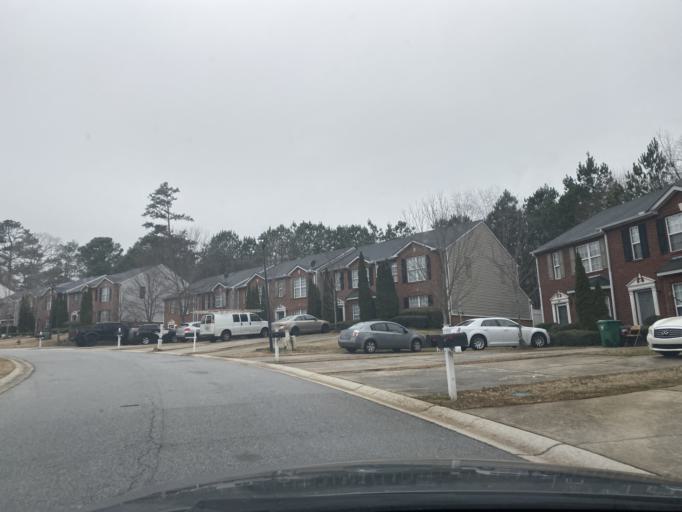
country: US
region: Georgia
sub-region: DeKalb County
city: Pine Mountain
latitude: 33.7003
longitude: -84.1550
